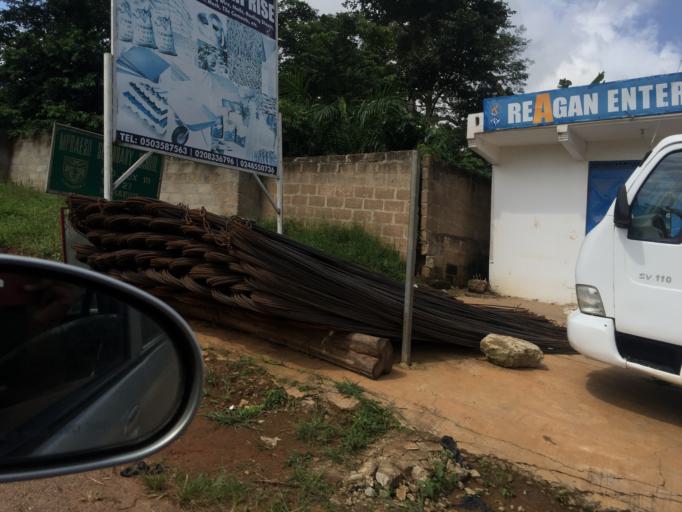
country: GH
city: Mpraeso
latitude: 6.5987
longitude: -0.7392
